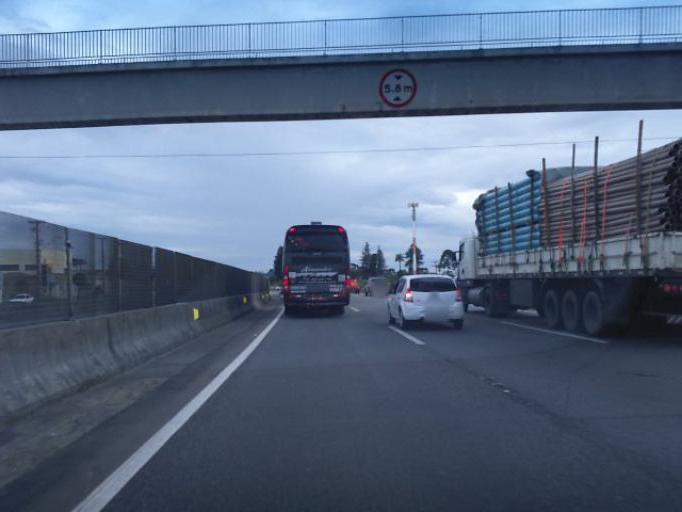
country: BR
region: Parana
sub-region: Sao Jose Dos Pinhais
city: Sao Jose dos Pinhais
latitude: -25.6112
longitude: -49.1716
